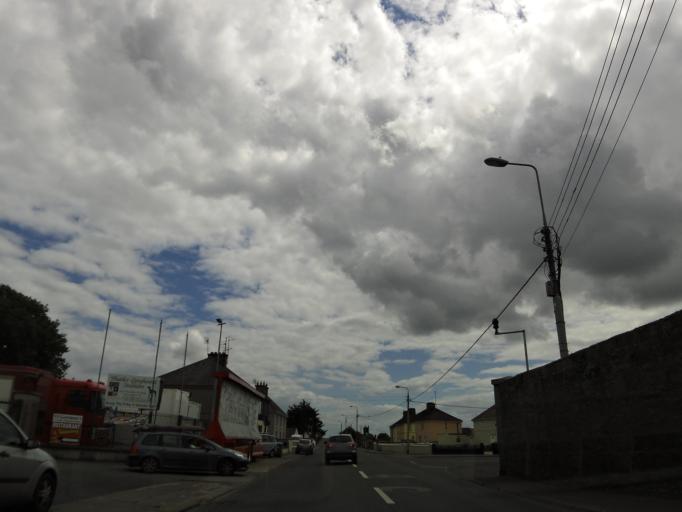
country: IE
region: Munster
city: Thurles
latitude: 52.6834
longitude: -7.8234
